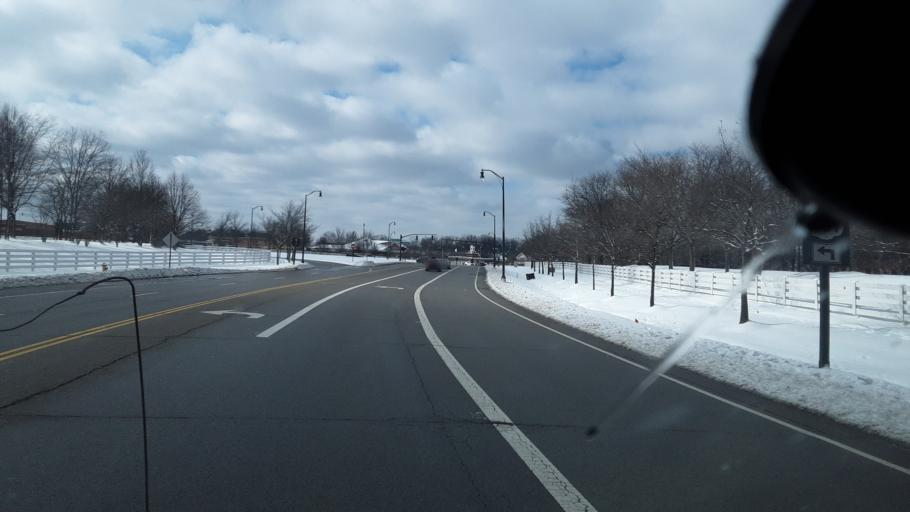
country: US
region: Ohio
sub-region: Franklin County
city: New Albany
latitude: 40.0948
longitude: -82.8206
